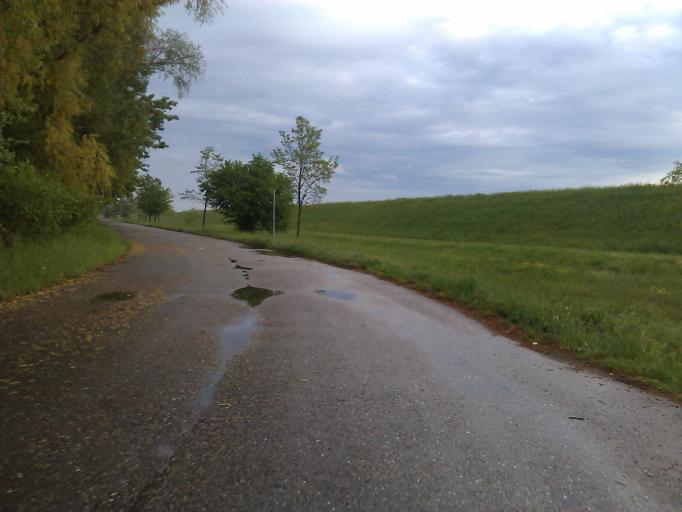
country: FR
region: Alsace
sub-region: Departement du Bas-Rhin
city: Drusenheim
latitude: 48.7419
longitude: 7.9693
